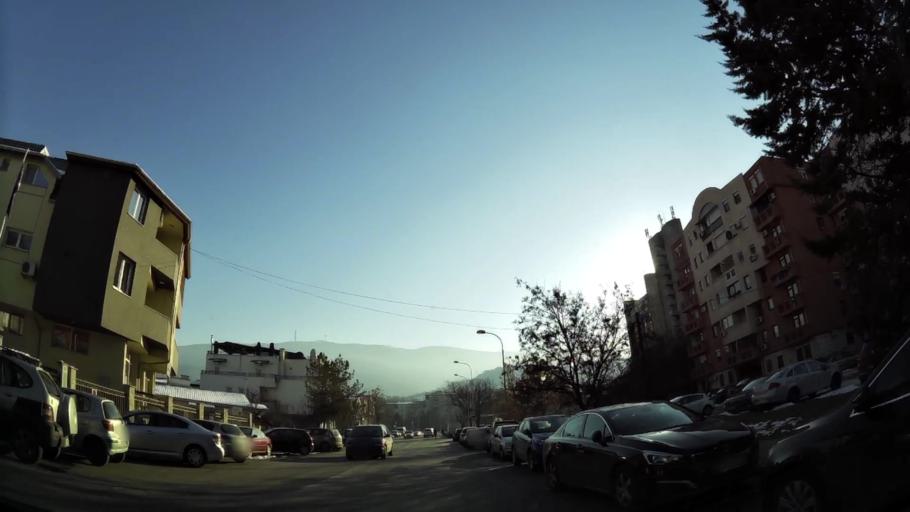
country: MK
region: Karpos
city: Skopje
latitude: 42.0001
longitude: 21.3917
